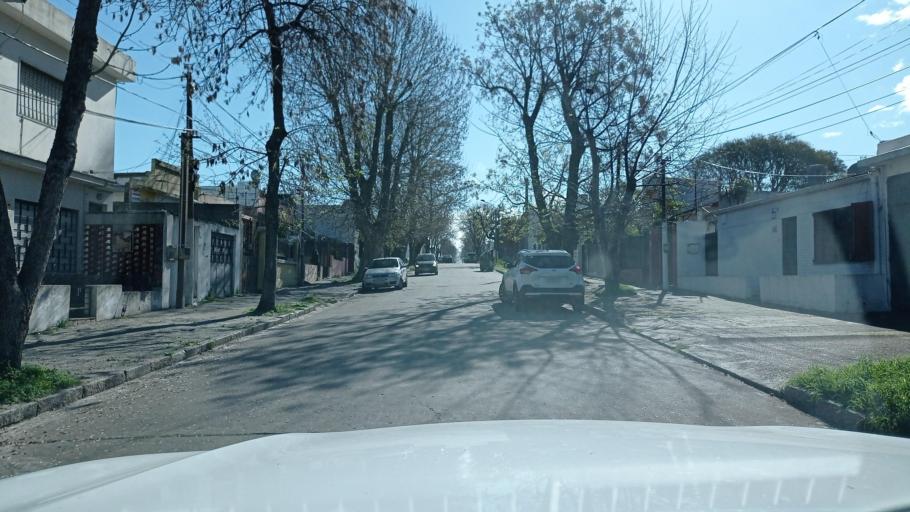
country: UY
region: Montevideo
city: Montevideo
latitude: -34.8541
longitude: -56.1642
